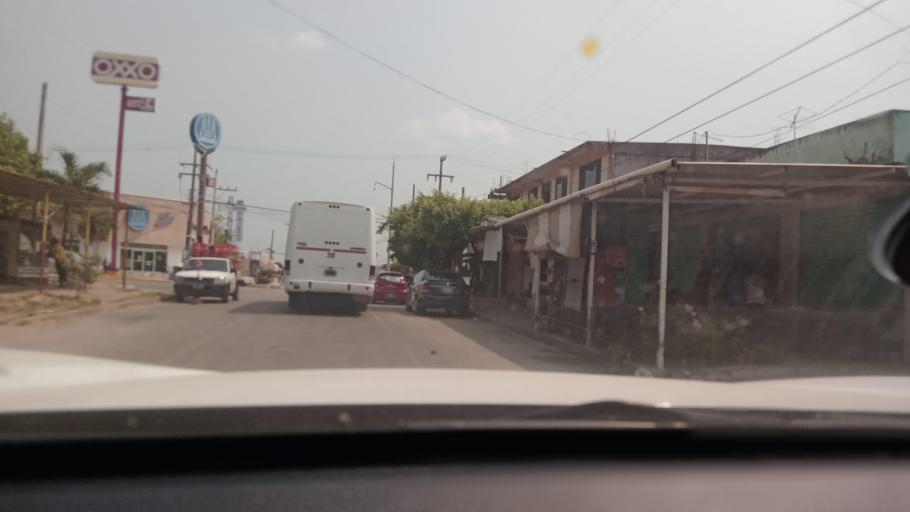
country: MX
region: Veracruz
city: Minatitlan
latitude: 17.9805
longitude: -94.5688
